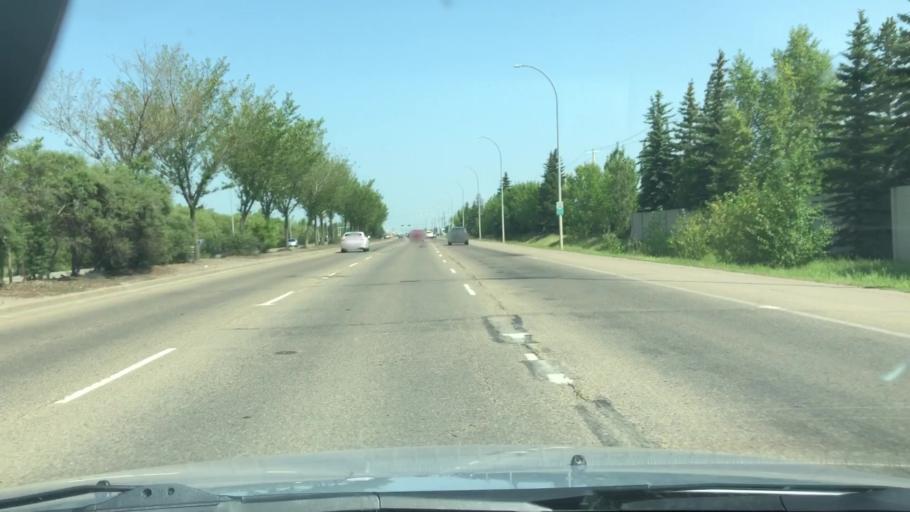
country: CA
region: Alberta
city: Edmonton
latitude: 53.6103
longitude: -113.4917
